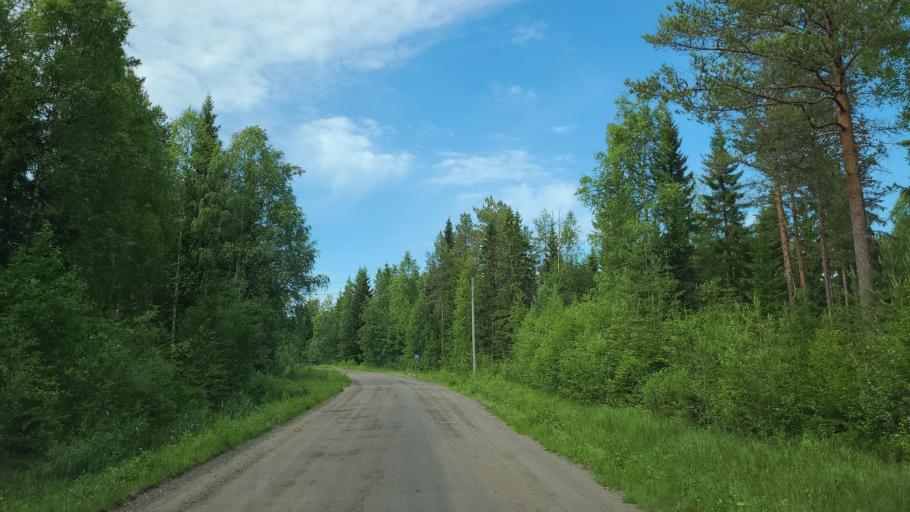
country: SE
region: Vaesterbotten
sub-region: Robertsfors Kommun
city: Robertsfors
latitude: 64.1645
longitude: 20.9703
